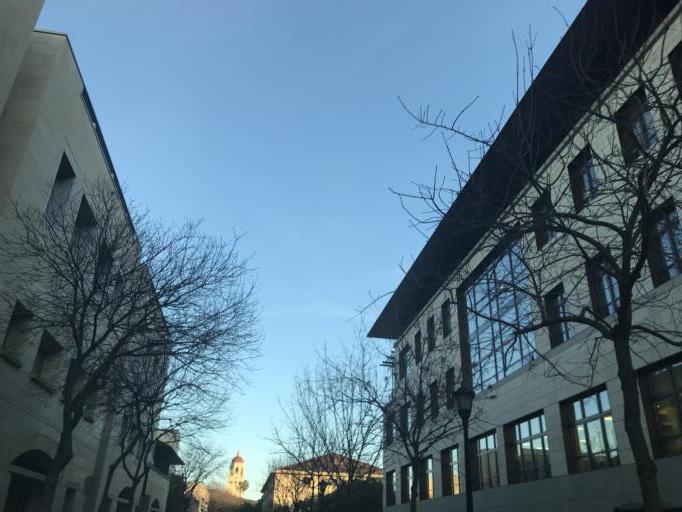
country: US
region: California
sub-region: Santa Clara County
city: Stanford
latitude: 37.4290
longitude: -122.1741
